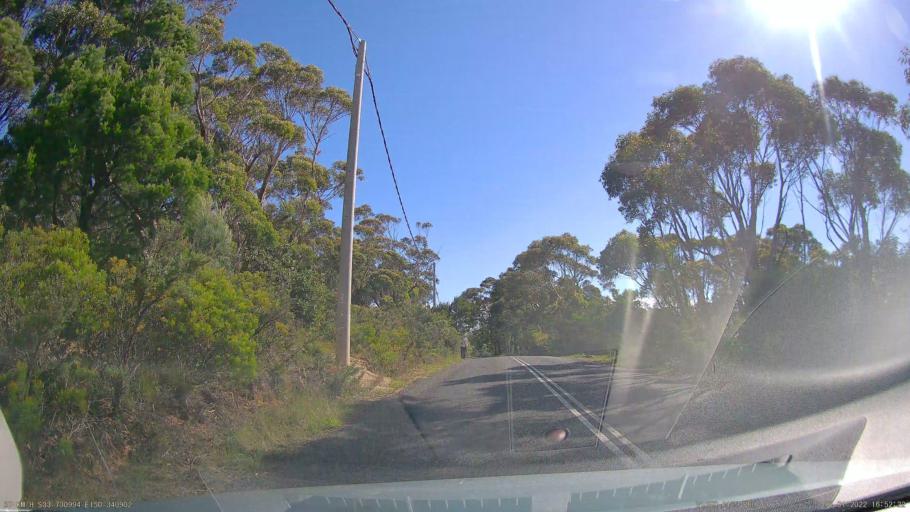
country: AU
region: New South Wales
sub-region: Blue Mountains Municipality
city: Leura
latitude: -33.7311
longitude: 150.3408
